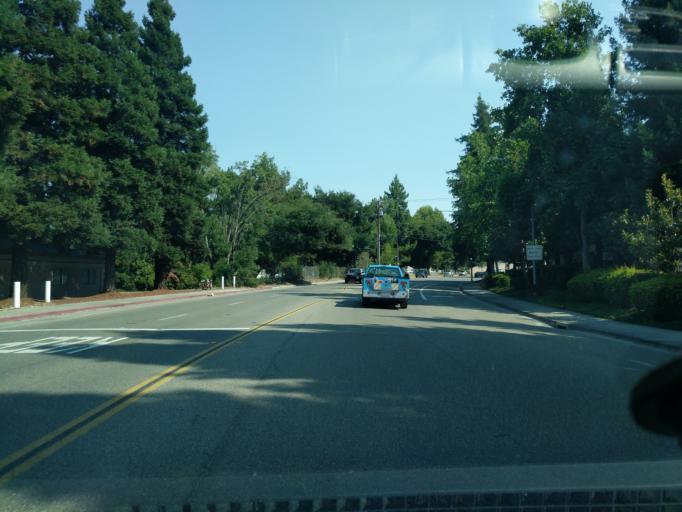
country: US
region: California
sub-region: Contra Costa County
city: Danville
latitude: 37.8091
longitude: -121.9929
